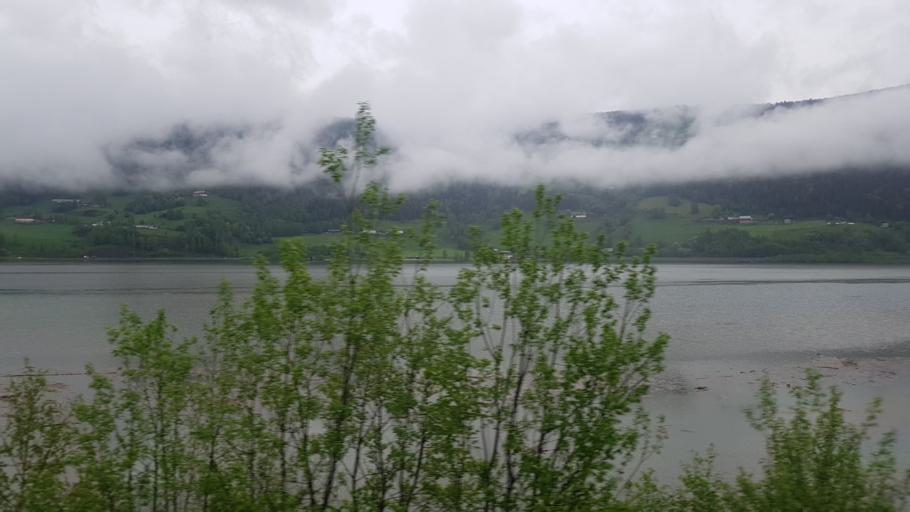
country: NO
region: Oppland
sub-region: Ringebu
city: Ringebu
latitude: 61.4307
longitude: 10.1897
